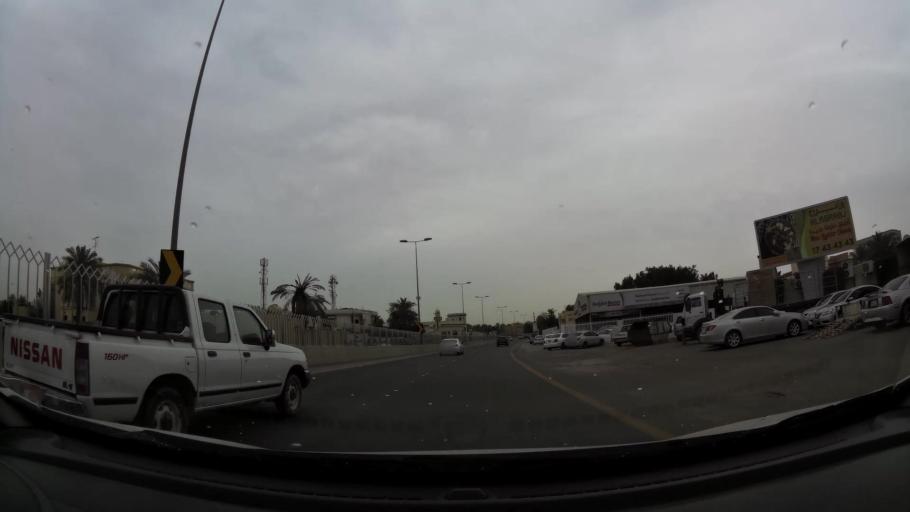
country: BH
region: Manama
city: Jidd Hafs
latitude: 26.2150
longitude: 50.5338
